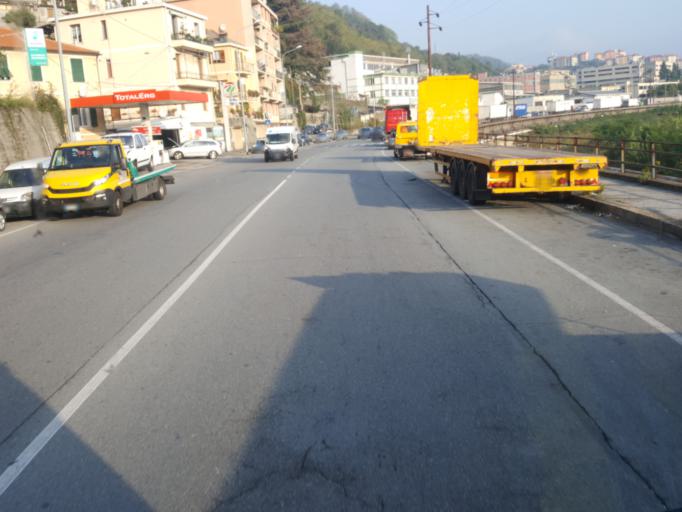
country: IT
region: Liguria
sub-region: Provincia di Genova
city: Manesseno
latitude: 44.4618
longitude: 8.8971
